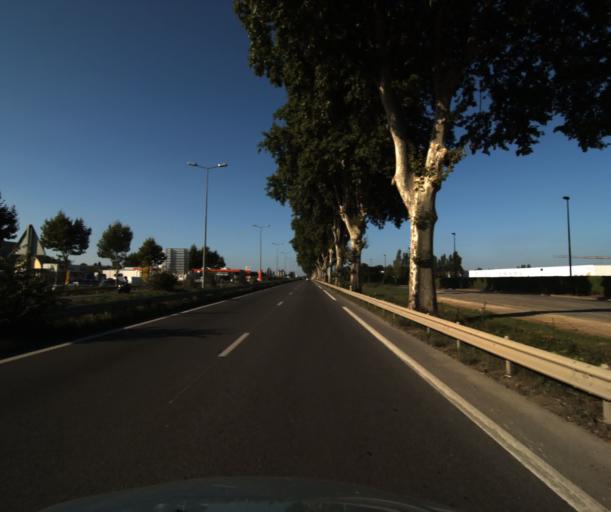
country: FR
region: Midi-Pyrenees
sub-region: Departement de la Haute-Garonne
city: Saubens
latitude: 43.4801
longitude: 1.3360
